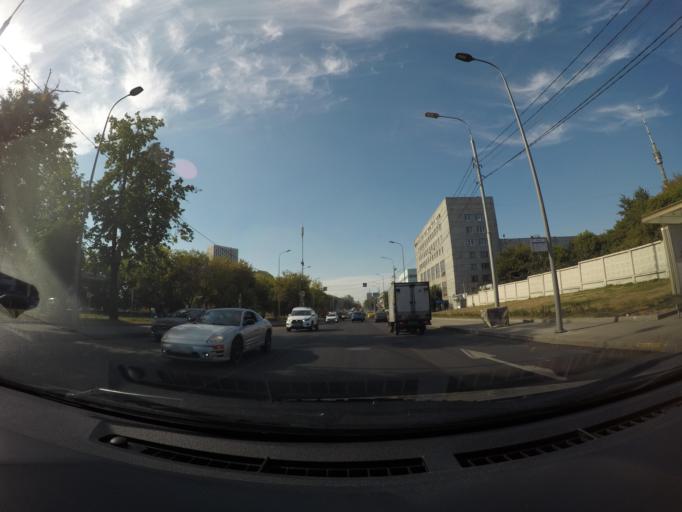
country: RU
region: Moscow
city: Mar'ina Roshcha
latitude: 55.8107
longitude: 37.6069
